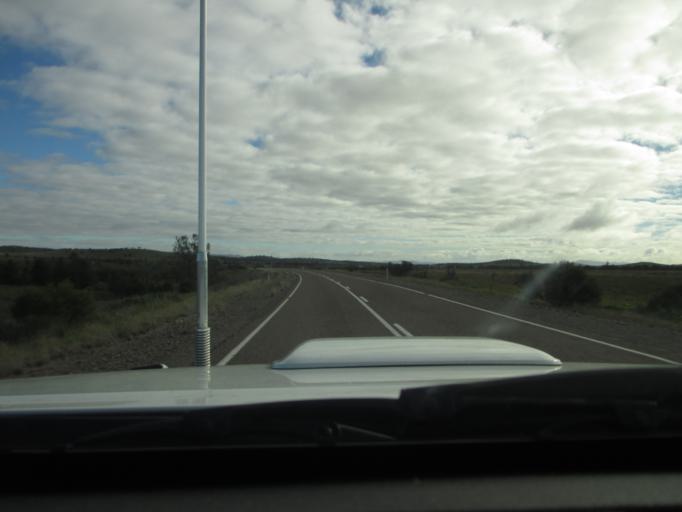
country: AU
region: South Australia
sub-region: Peterborough
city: Peterborough
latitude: -32.5340
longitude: 138.5557
